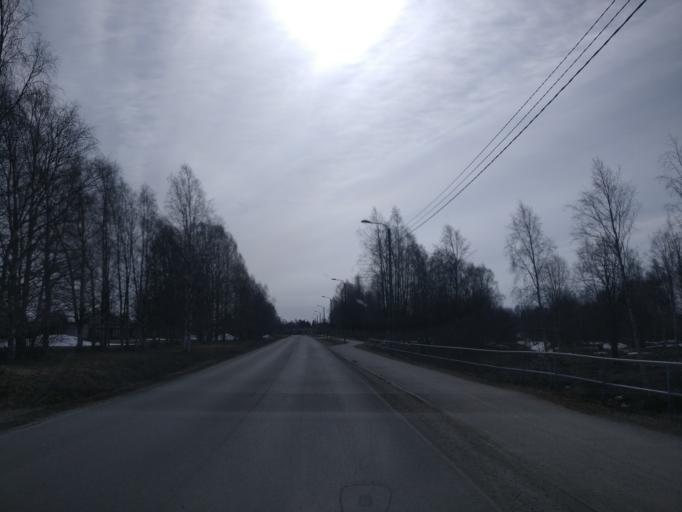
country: FI
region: Lapland
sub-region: Kemi-Tornio
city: Kemi
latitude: 65.7544
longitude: 24.5509
